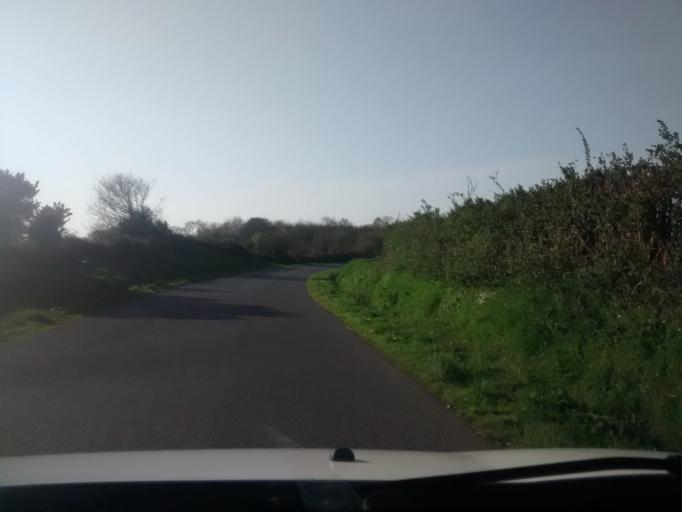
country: FR
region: Brittany
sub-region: Departement des Cotes-d'Armor
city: Trevou-Treguignec
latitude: 48.7944
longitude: -3.3462
